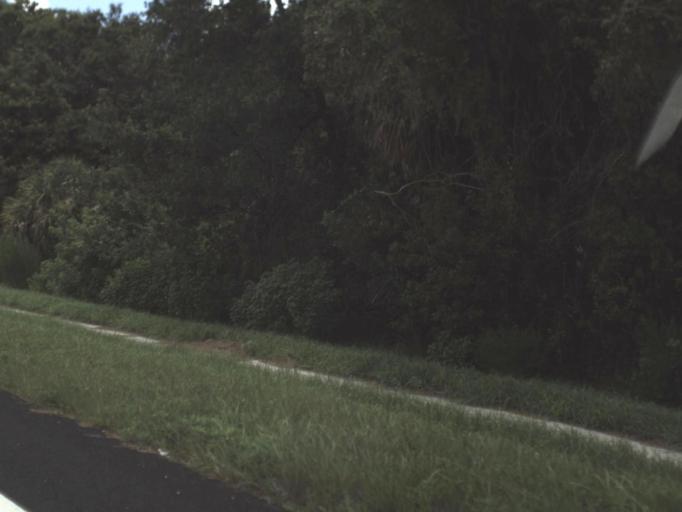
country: US
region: Florida
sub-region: Hillsborough County
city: Lutz
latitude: 28.1673
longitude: -82.4772
